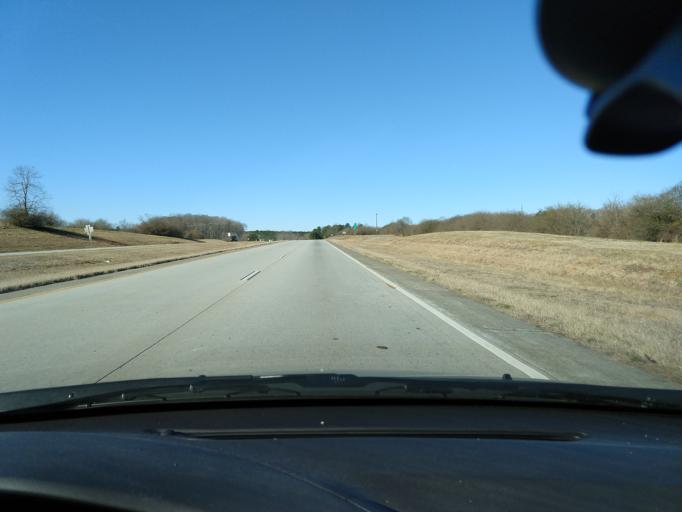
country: US
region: Georgia
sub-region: Barrow County
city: Statham
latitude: 33.9614
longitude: -83.6300
